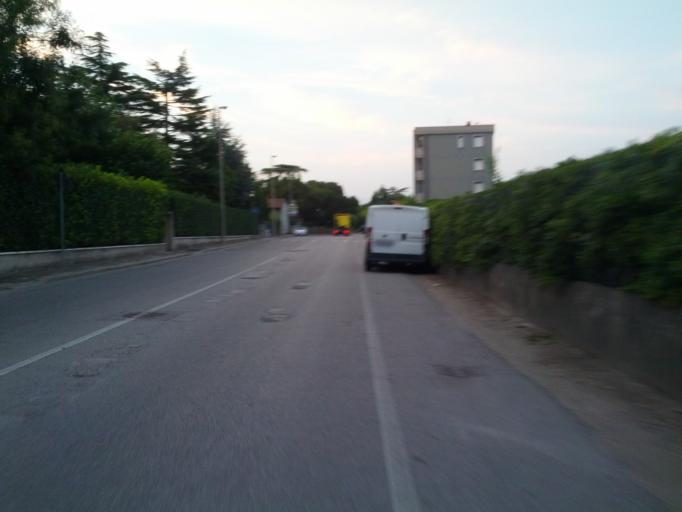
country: IT
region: Veneto
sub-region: Provincia di Verona
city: Verona
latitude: 45.4130
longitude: 10.9671
